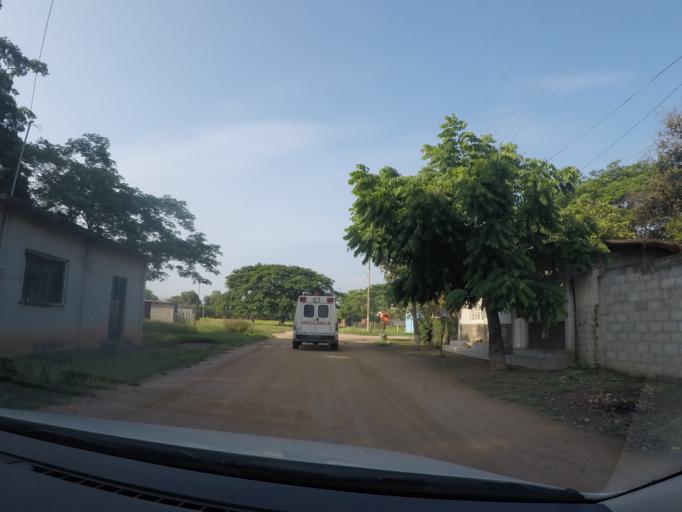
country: MX
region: Oaxaca
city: San Francisco Ixhuatan
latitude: 16.3365
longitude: -94.5212
